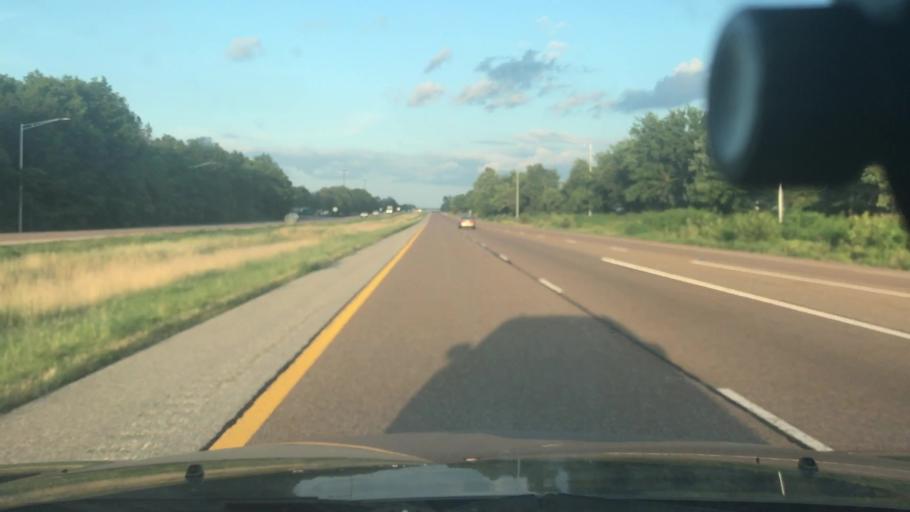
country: US
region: Illinois
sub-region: Saint Clair County
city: Mascoutah
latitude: 38.5488
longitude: -89.7696
